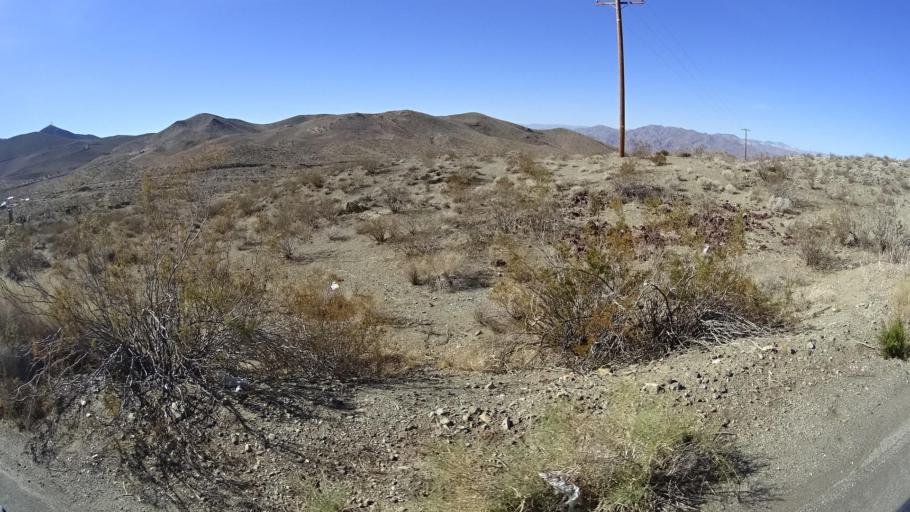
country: US
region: California
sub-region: Kern County
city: Ridgecrest
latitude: 35.3739
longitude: -117.6552
